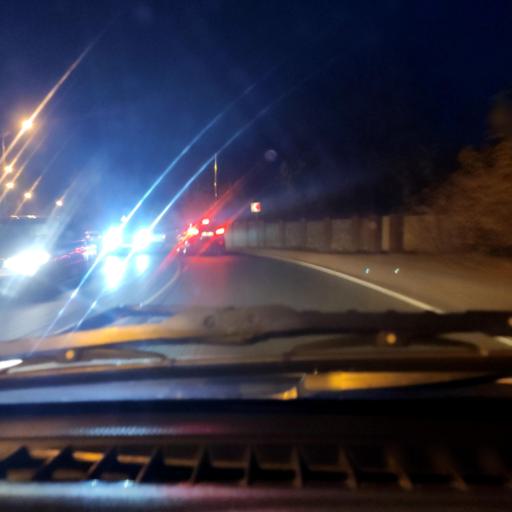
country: RU
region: Samara
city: Tol'yatti
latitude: 53.4888
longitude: 49.3079
